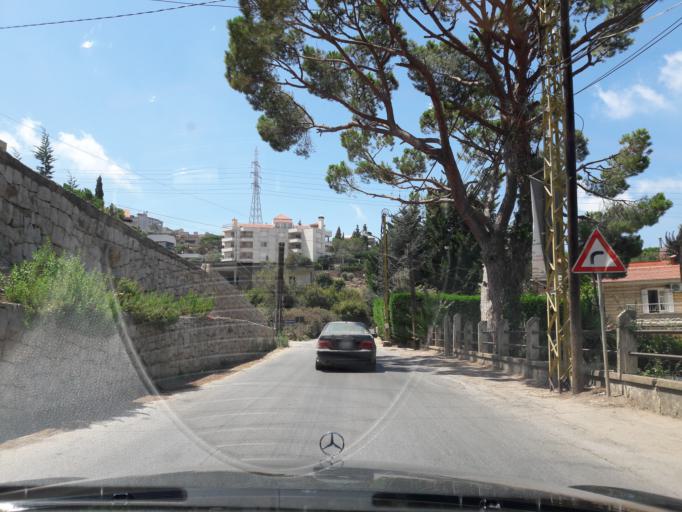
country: LB
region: Mont-Liban
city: Djounie
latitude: 33.9252
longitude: 35.6574
